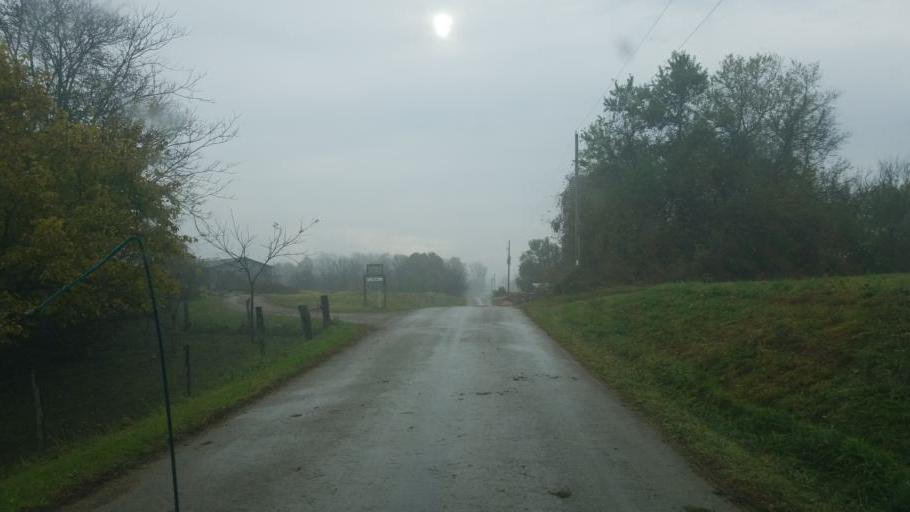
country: US
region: Ohio
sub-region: Morgan County
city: McConnelsville
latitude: 39.5178
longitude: -81.8343
